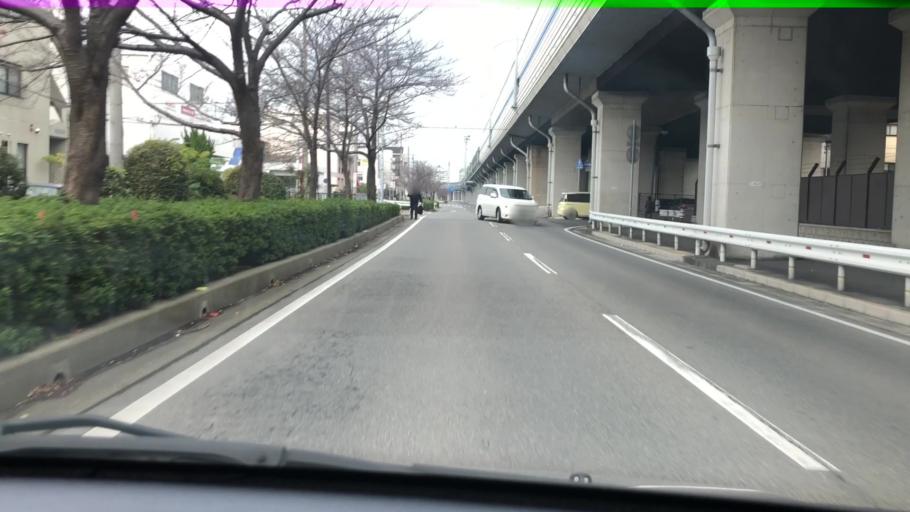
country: JP
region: Hyogo
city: Nishinomiya-hama
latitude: 34.7305
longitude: 135.3579
